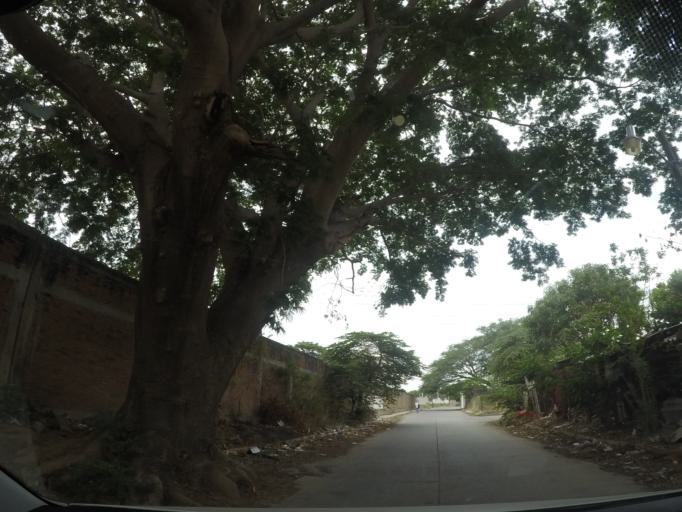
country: MX
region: Oaxaca
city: Juchitan de Zaragoza
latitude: 16.4504
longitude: -95.0147
